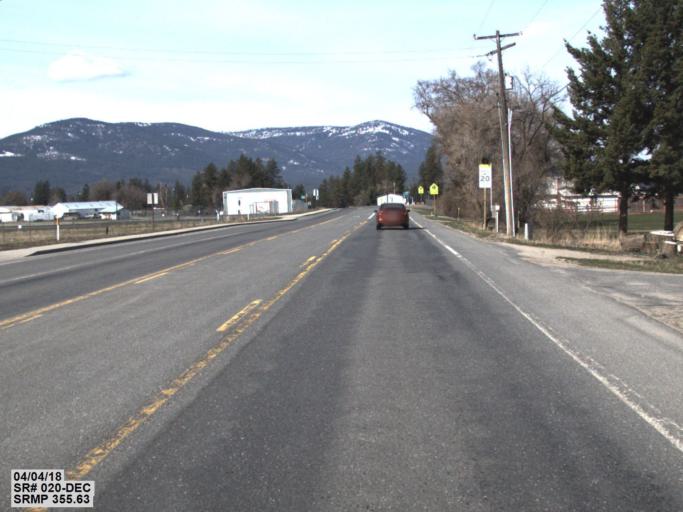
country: US
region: Washington
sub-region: Stevens County
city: Colville
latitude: 48.5473
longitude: -117.8779
